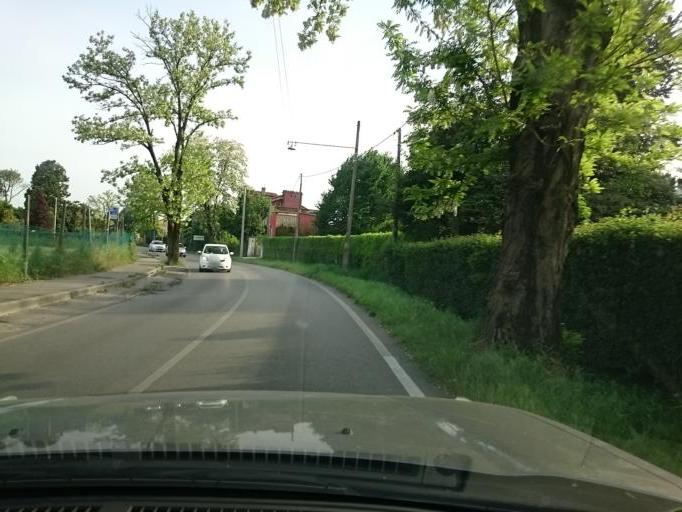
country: IT
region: Veneto
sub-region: Provincia di Padova
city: Noventa
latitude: 45.4046
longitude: 11.9446
